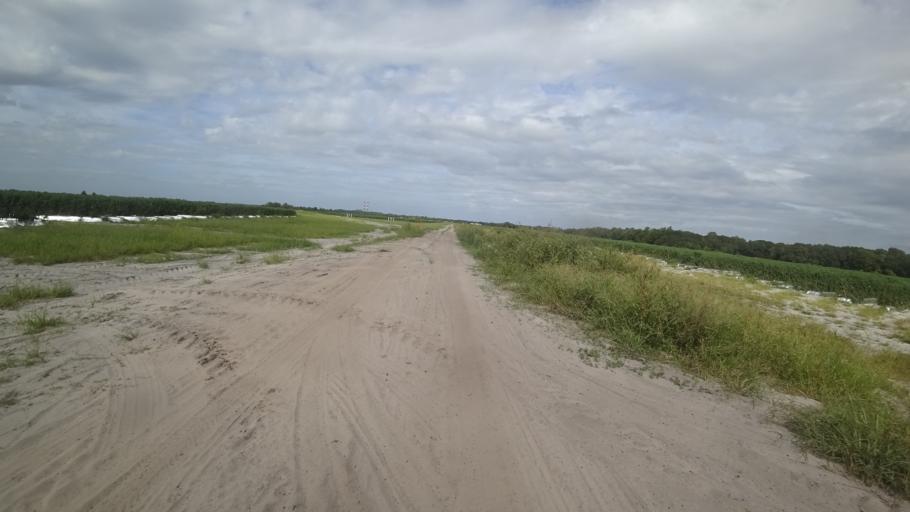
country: US
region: Florida
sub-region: Hillsborough County
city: Wimauma
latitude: 27.5887
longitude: -82.3055
